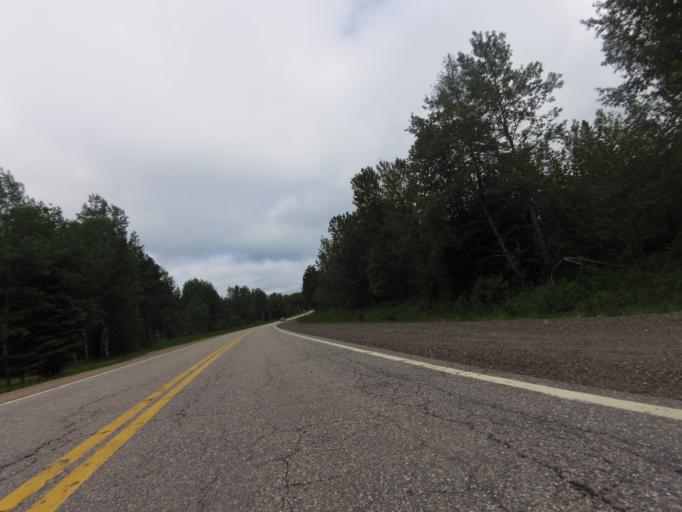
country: CA
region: Quebec
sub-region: Outaouais
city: Shawville
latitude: 45.9076
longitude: -76.3085
